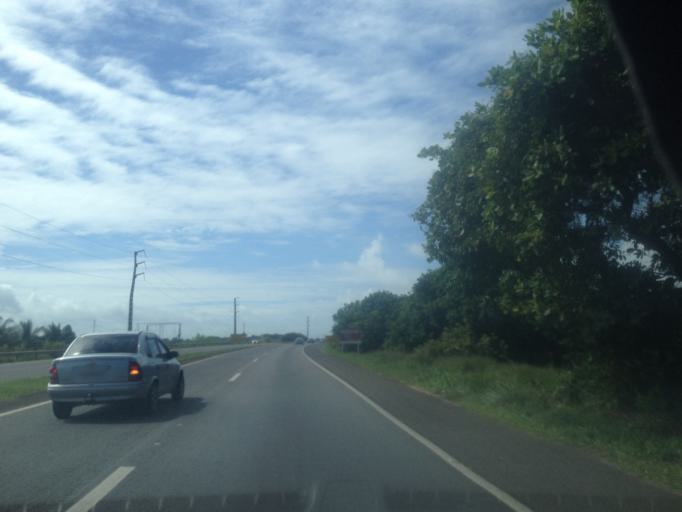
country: BR
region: Bahia
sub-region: Camacari
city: Camacari
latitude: -12.6518
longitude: -38.0840
